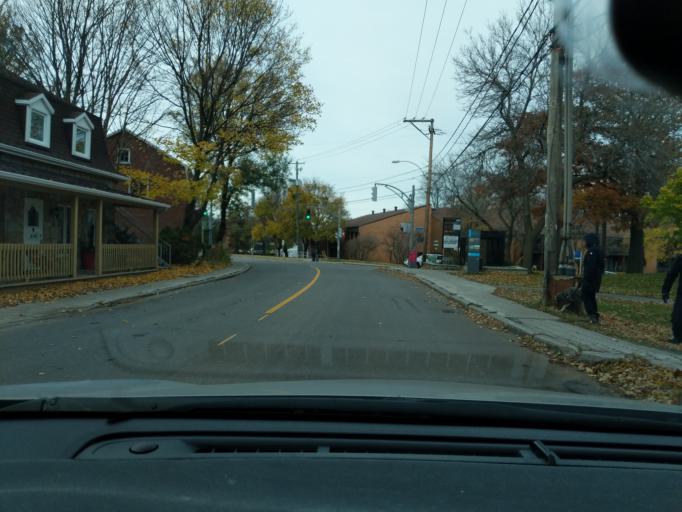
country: CA
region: Quebec
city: Quebec
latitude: 46.7824
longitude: -71.2462
